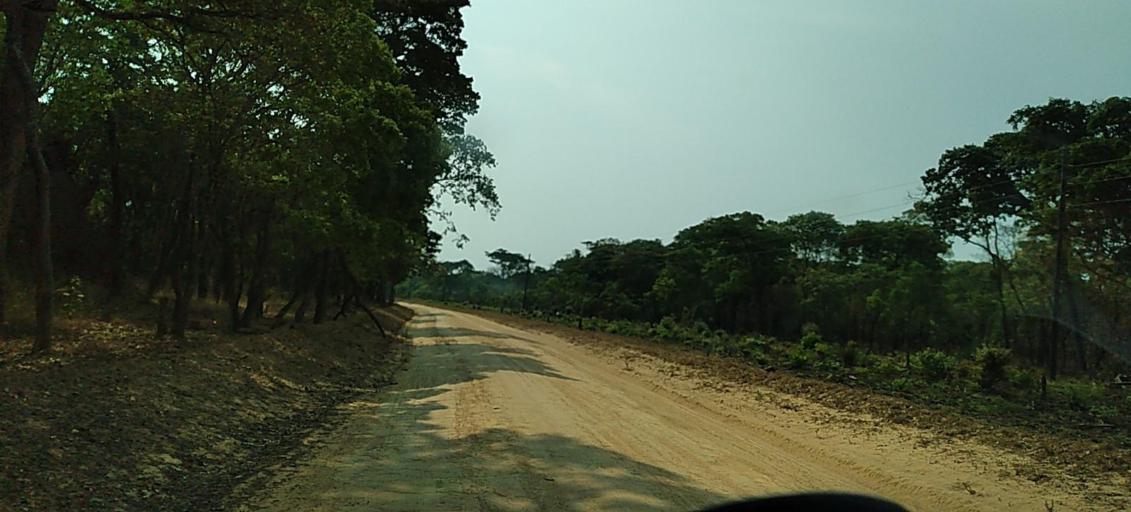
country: ZM
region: North-Western
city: Solwezi
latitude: -12.6825
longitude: 26.3868
